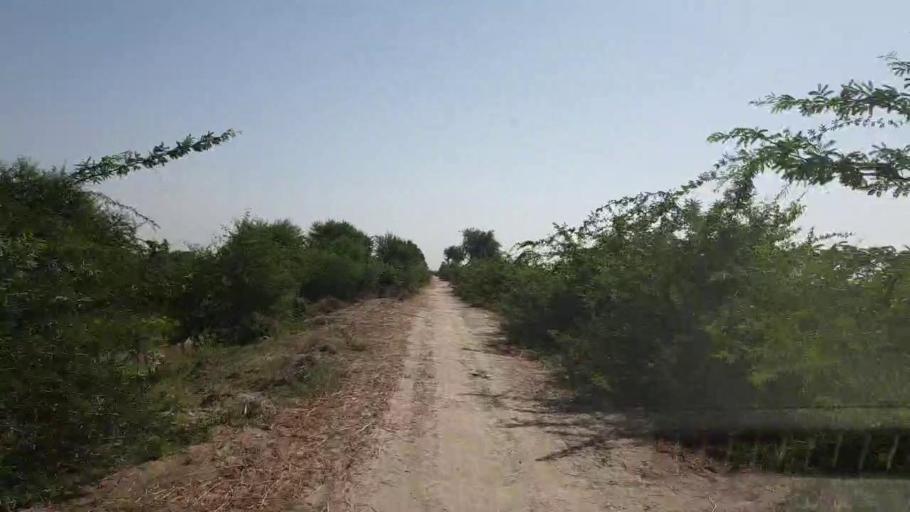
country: PK
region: Sindh
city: Kadhan
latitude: 24.6221
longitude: 68.9957
